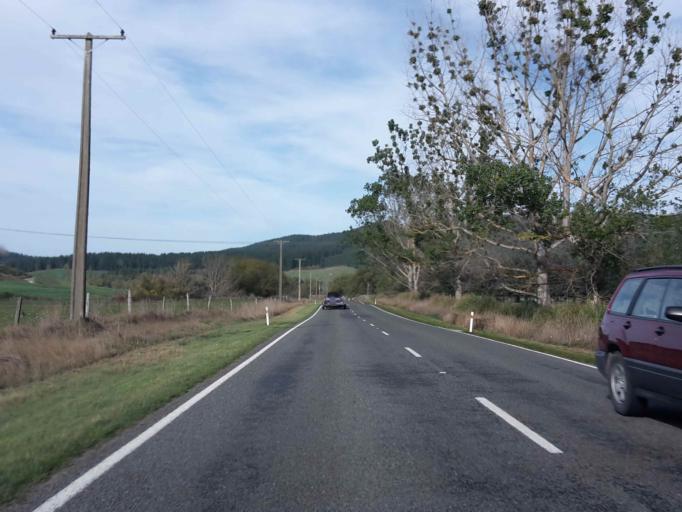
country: NZ
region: Canterbury
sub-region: Timaru District
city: Pleasant Point
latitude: -44.1209
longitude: 171.0328
